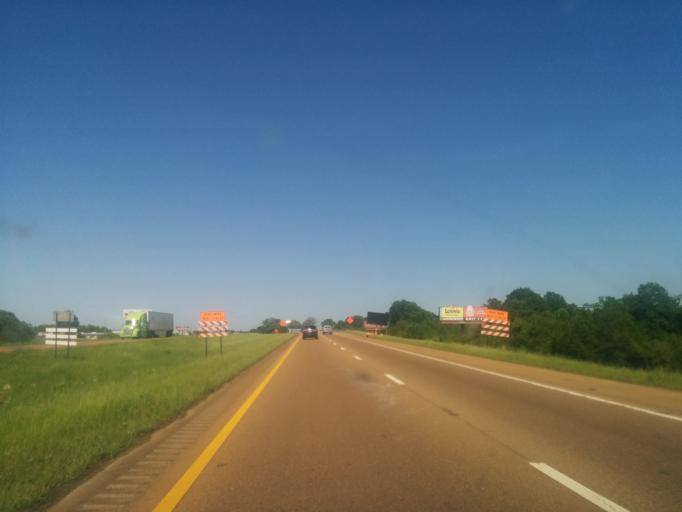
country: US
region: Mississippi
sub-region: Madison County
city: Madison
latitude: 32.5073
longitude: -90.1125
